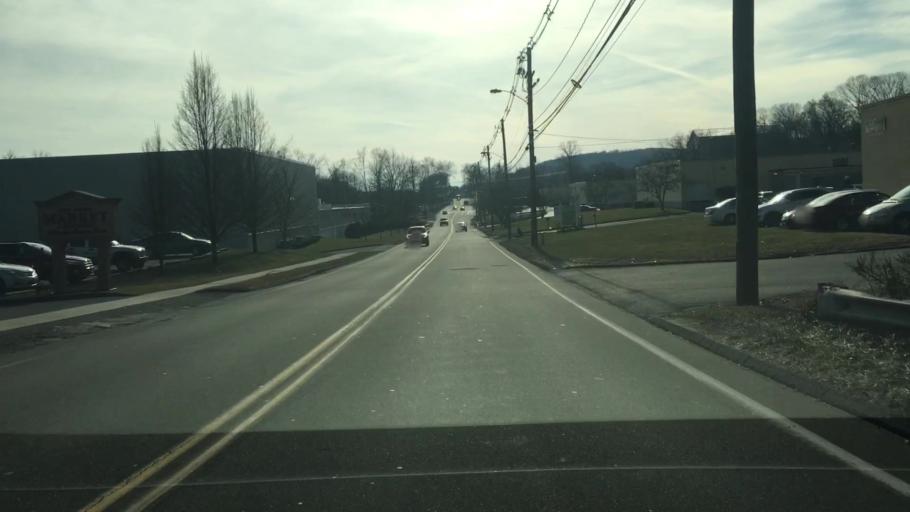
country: US
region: Connecticut
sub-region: New Haven County
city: Wallingford
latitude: 41.4539
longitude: -72.8413
